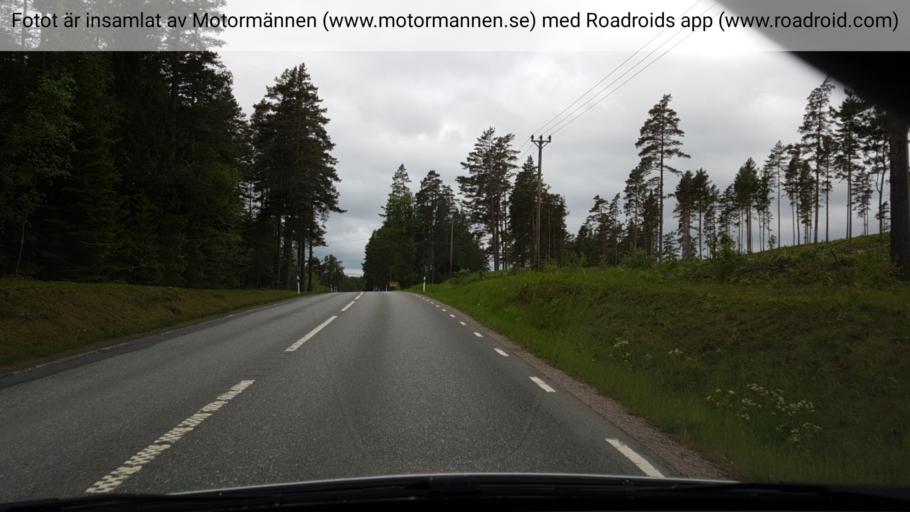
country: SE
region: Joenkoeping
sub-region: Jonkopings Kommun
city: Asa
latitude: 58.0152
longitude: 14.6781
